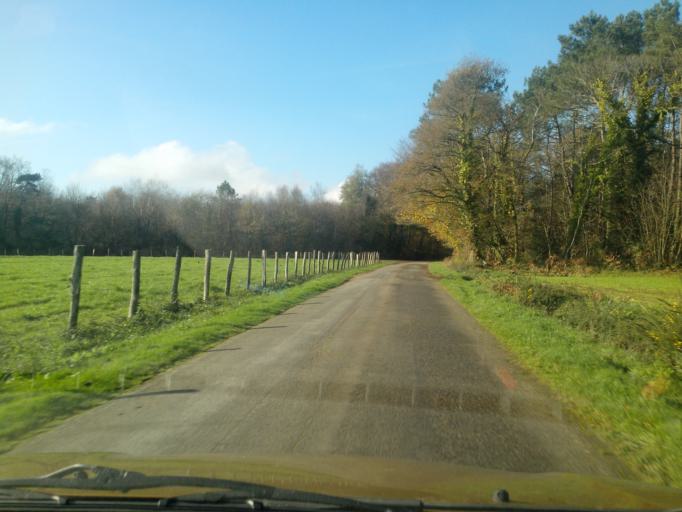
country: FR
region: Brittany
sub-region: Departement du Morbihan
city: Pluherlin
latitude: 47.7280
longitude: -2.3558
